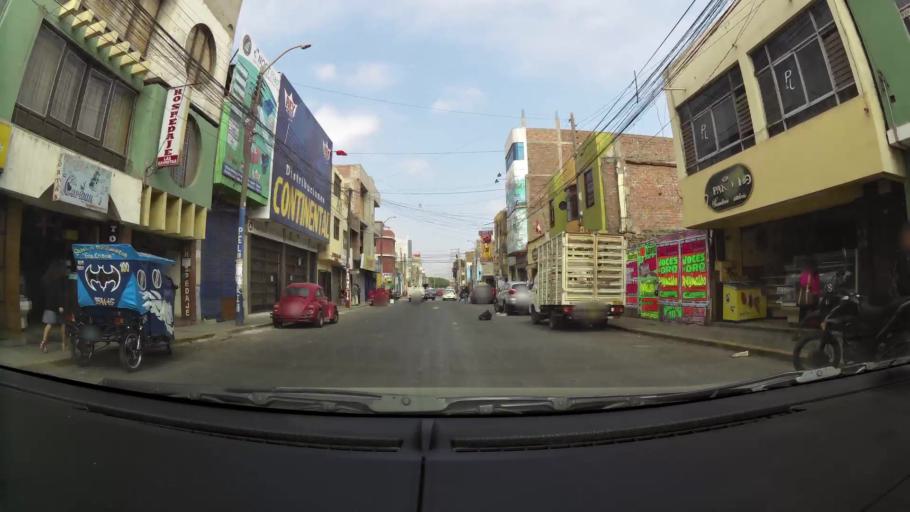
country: PE
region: La Libertad
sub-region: Provincia de Trujillo
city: Trujillo
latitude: -8.1148
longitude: -79.0224
